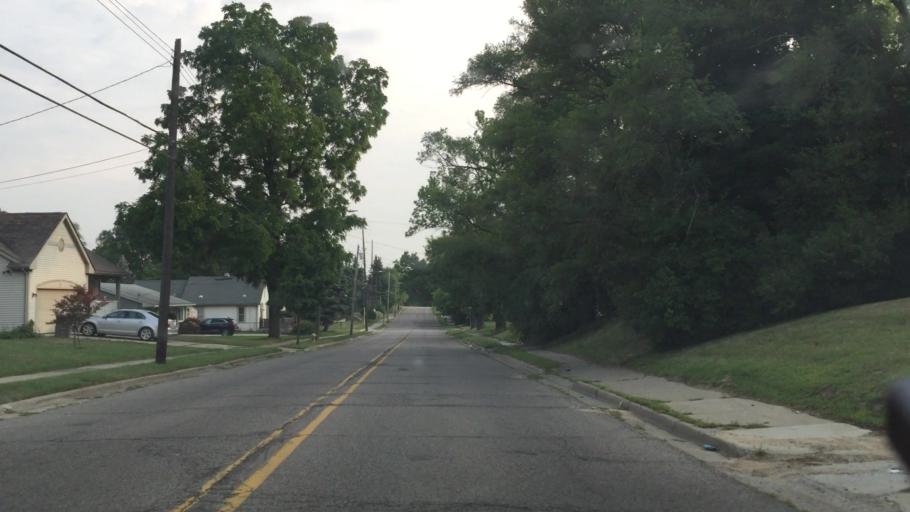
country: US
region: Michigan
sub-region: Oakland County
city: Pontiac
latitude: 42.6316
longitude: -83.2753
